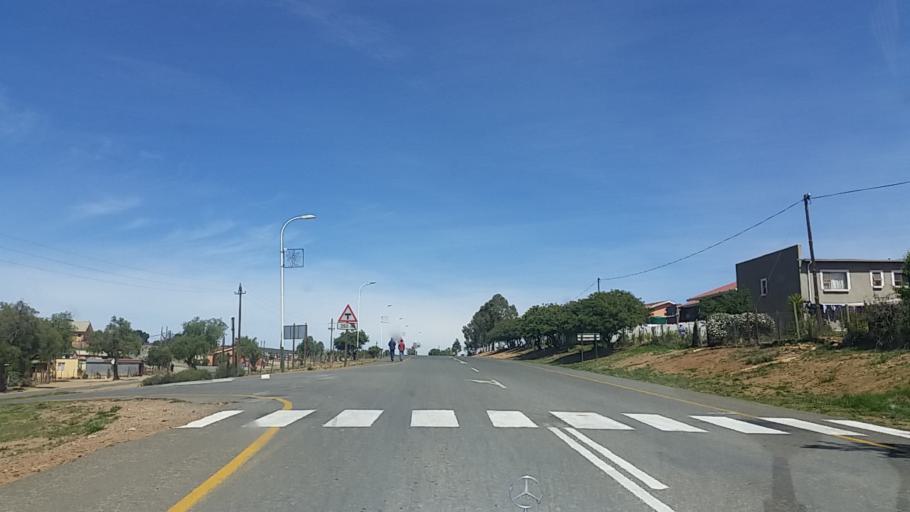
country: ZA
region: Western Cape
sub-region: Eden District Municipality
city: Knysna
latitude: -33.6601
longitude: 23.1149
